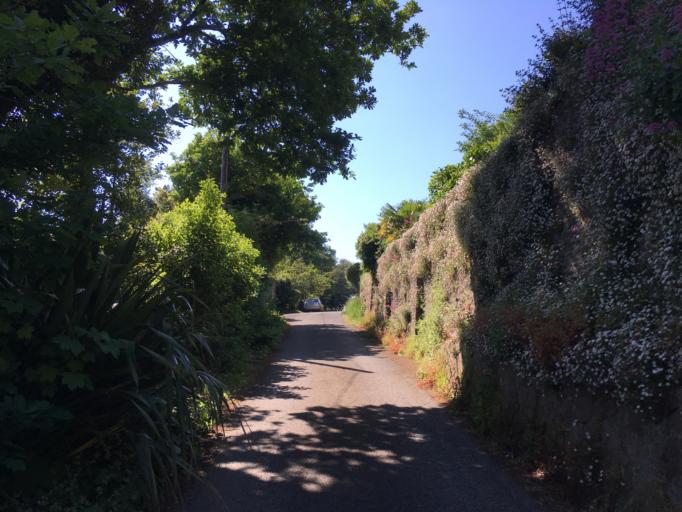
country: GB
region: England
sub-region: Devon
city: Dartmouth
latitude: 50.3475
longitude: -3.5679
